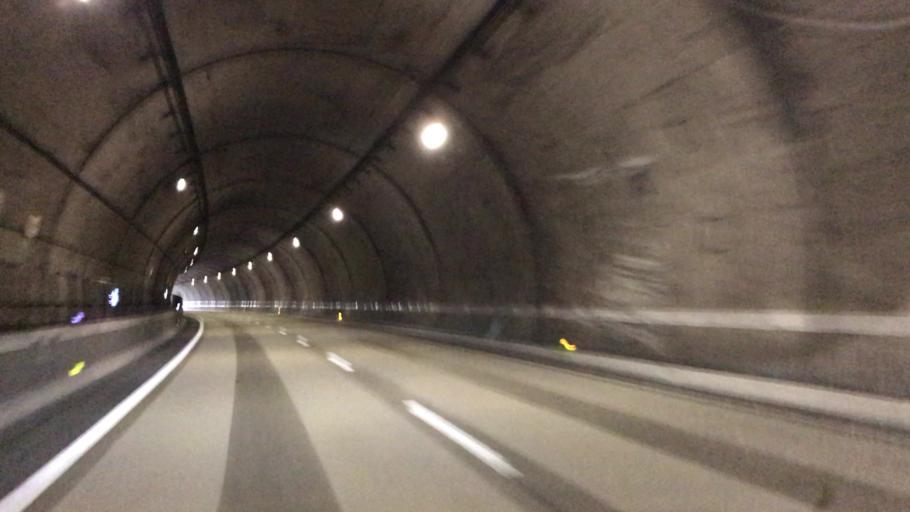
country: JP
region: Hyogo
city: Sandacho
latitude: 34.8084
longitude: 135.2441
